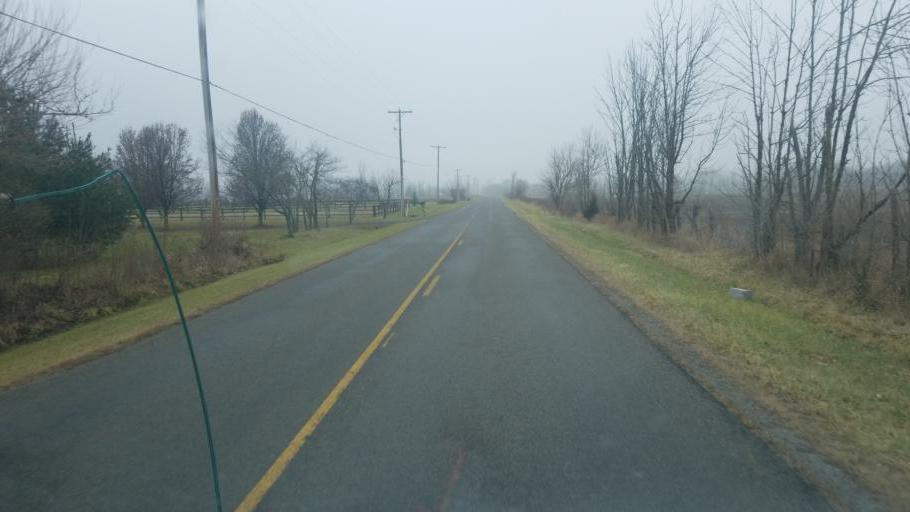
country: US
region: Ohio
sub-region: Champaign County
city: North Lewisburg
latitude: 40.3556
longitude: -83.5535
